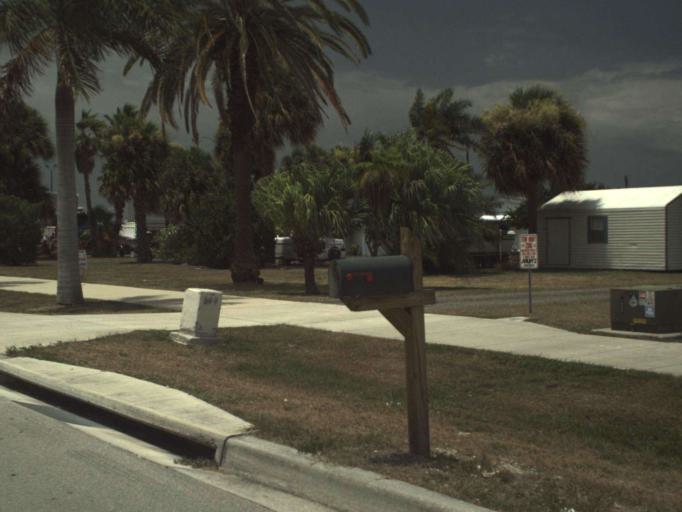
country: US
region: Florida
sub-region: Saint Lucie County
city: Fort Pierce
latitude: 27.4629
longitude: -80.3055
